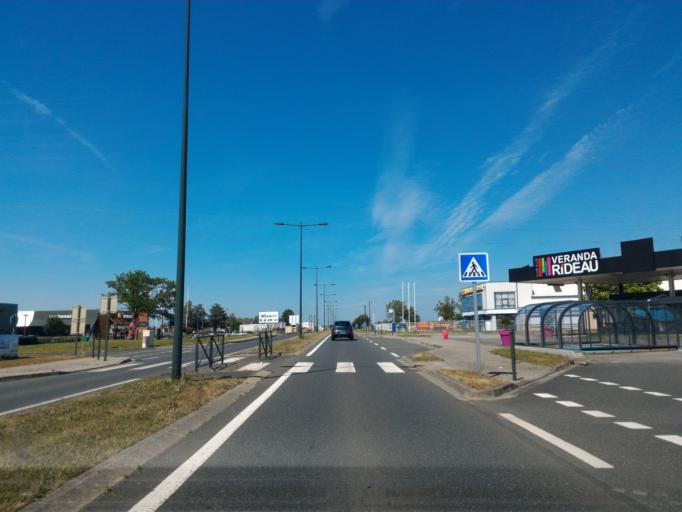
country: FR
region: Centre
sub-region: Departement de l'Indre
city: Saint-Maur
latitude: 46.7847
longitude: 1.6566
